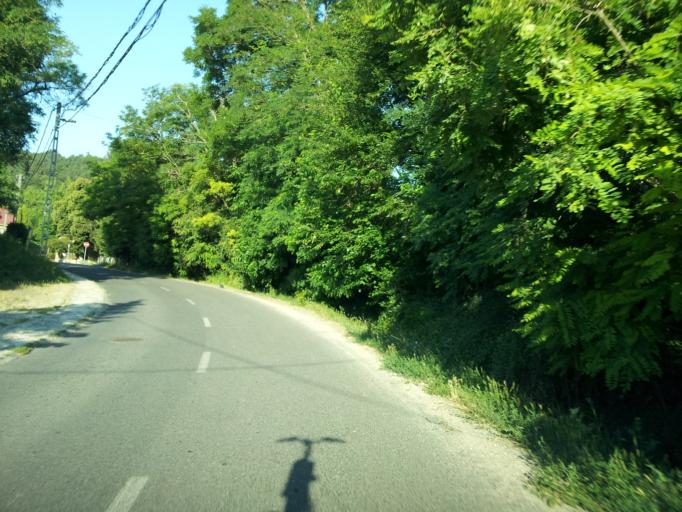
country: HU
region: Fejer
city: Many
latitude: 47.5202
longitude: 18.6126
